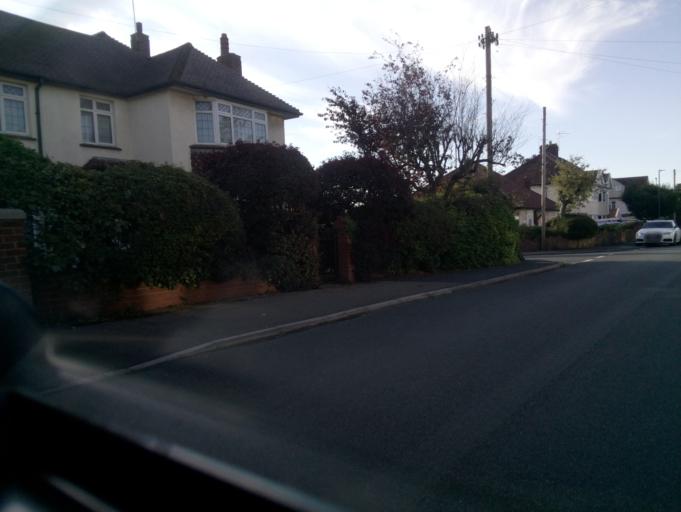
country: GB
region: England
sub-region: South Gloucestershire
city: Mangotsfield
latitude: 51.4943
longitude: -2.5035
